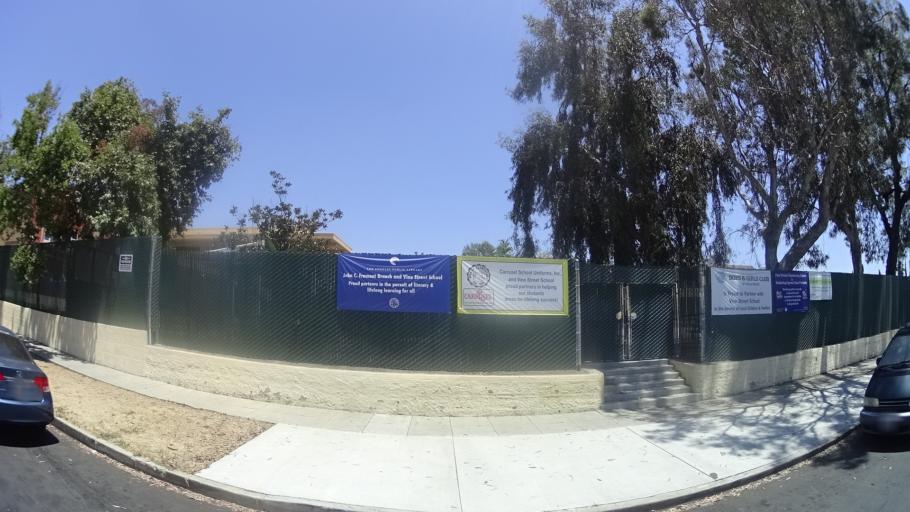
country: US
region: California
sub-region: Los Angeles County
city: Hollywood
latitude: 34.0881
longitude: -118.3277
